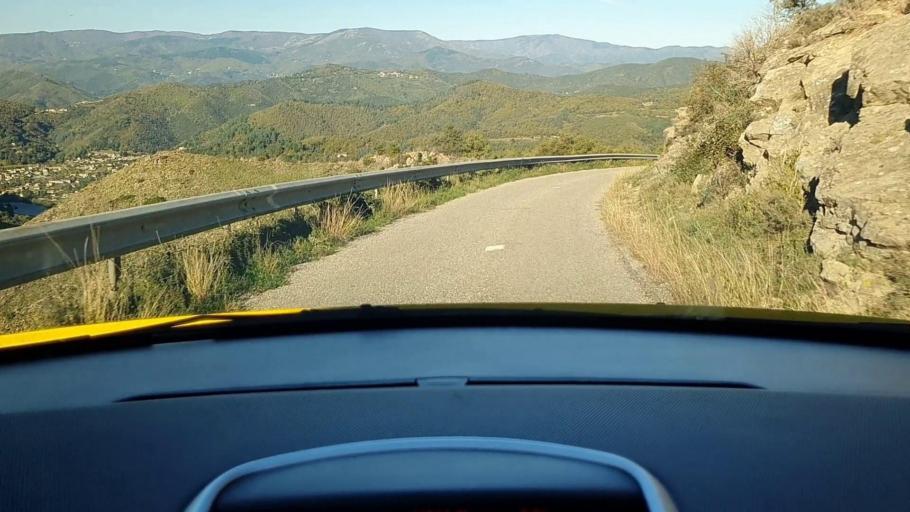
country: FR
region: Languedoc-Roussillon
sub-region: Departement du Gard
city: Sumene
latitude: 43.9783
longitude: 3.7497
